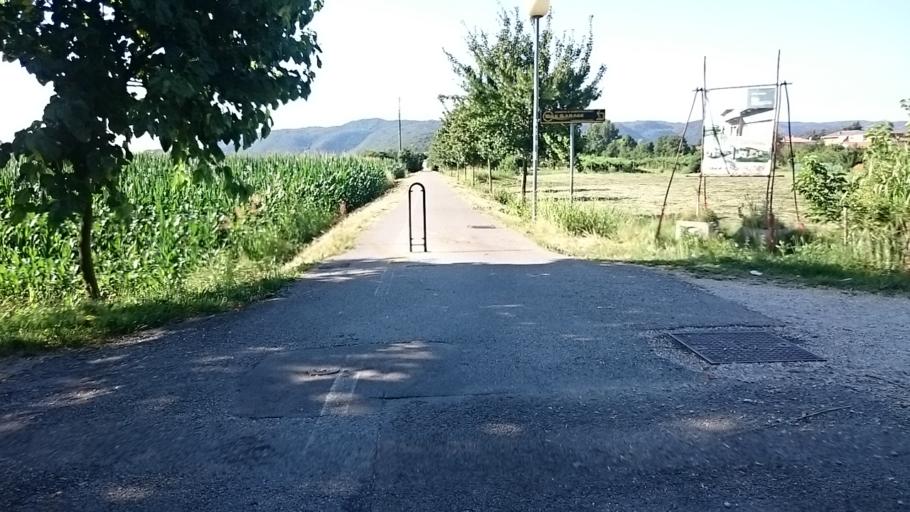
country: IT
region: Veneto
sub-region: Provincia di Vicenza
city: Arcugnano-Torri
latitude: 45.5140
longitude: 11.5683
